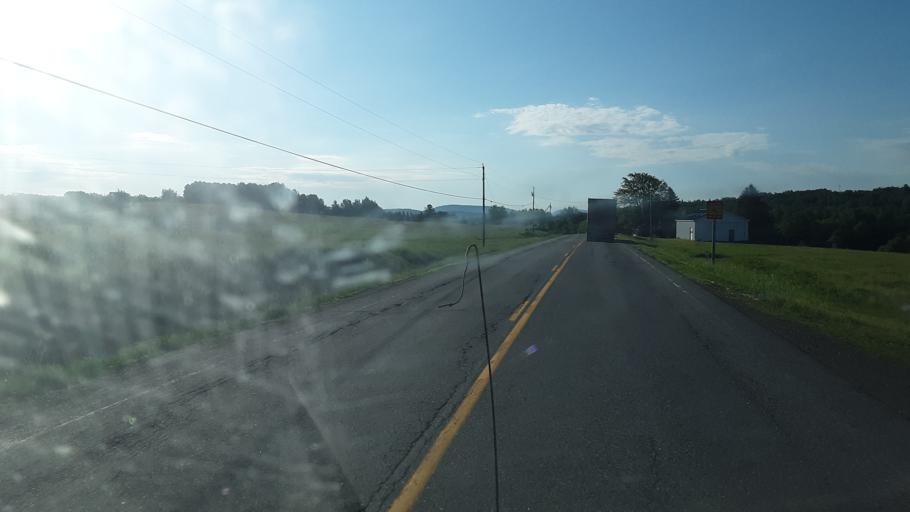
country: US
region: Maine
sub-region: Penobscot County
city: Patten
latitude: 46.1356
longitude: -68.1871
